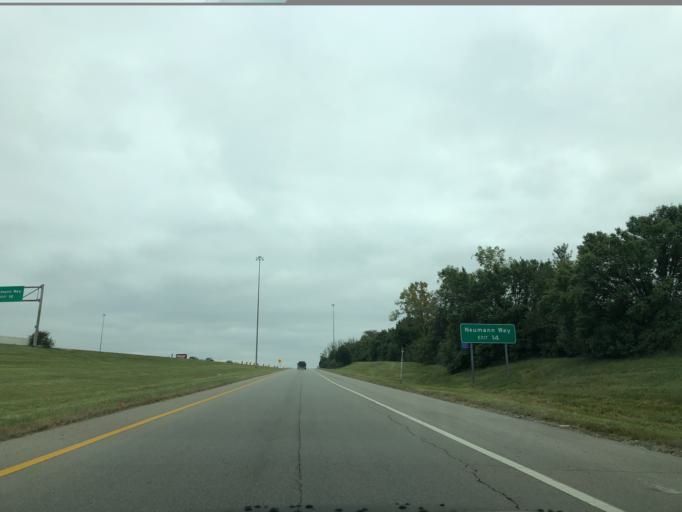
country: US
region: Ohio
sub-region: Hamilton County
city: Glendale
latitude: 39.2690
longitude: -84.4414
